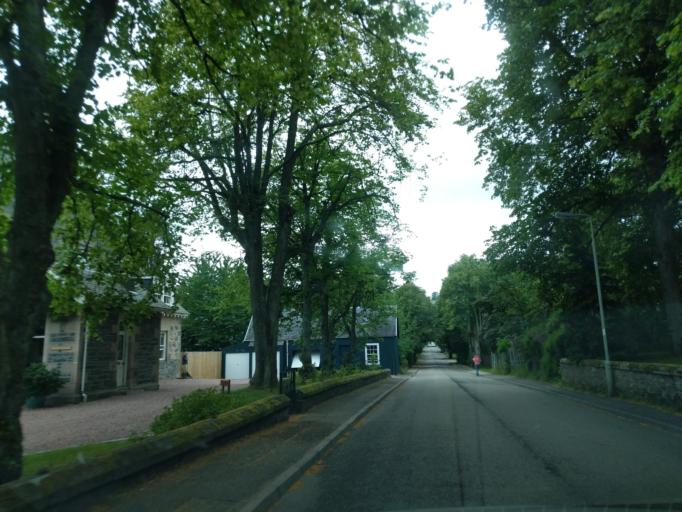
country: GB
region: Scotland
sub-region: Highland
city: Grantown on Spey
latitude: 57.3317
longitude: -3.6106
